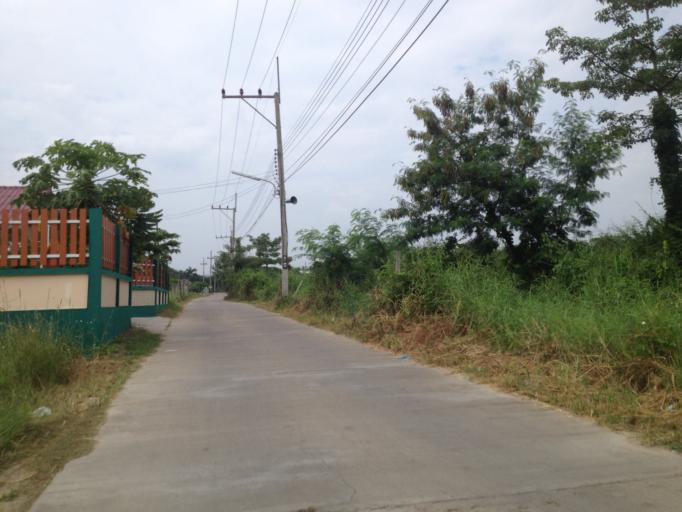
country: TH
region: Chiang Mai
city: San Pa Tong
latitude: 18.6575
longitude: 98.8734
